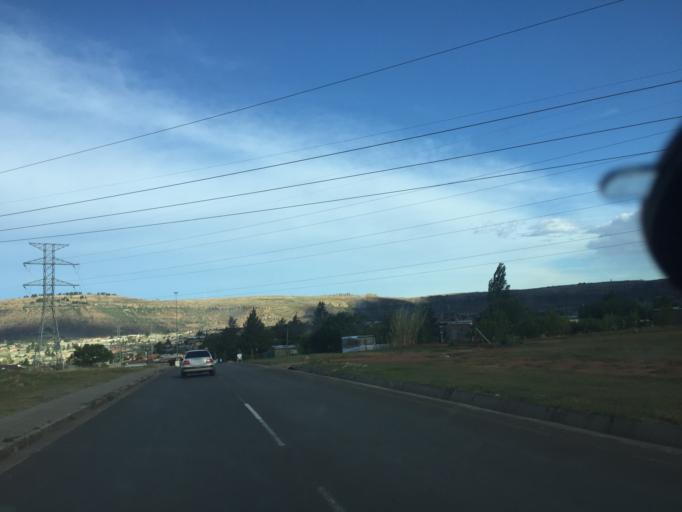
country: LS
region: Maseru
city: Maseru
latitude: -29.2831
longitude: 27.5390
